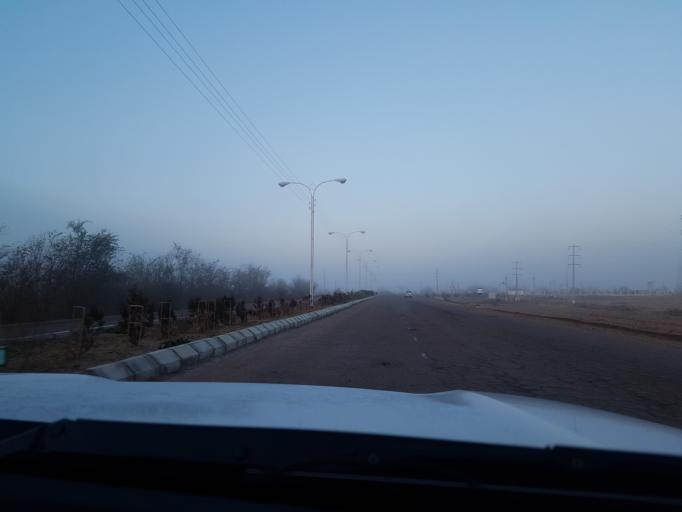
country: TM
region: Dasoguz
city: Koeneuergench
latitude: 41.7429
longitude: 58.6936
